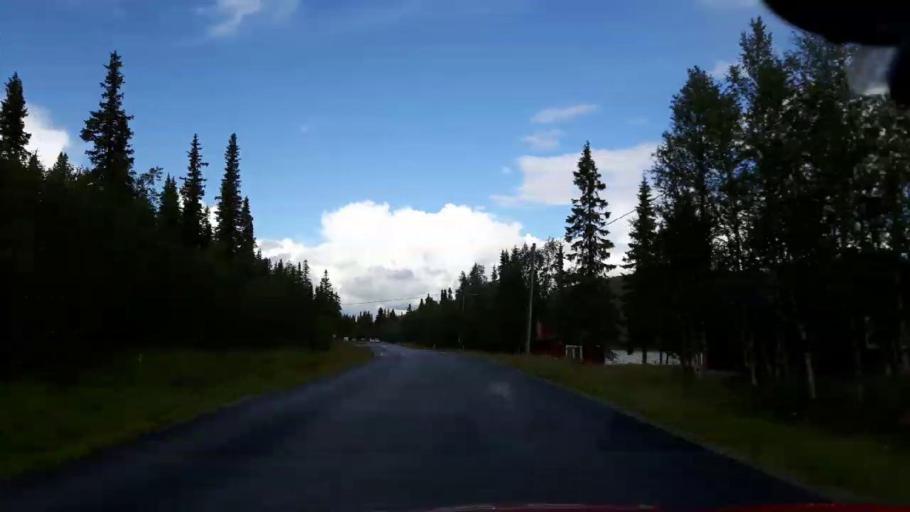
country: SE
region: Vaesterbotten
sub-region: Vilhelmina Kommun
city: Sjoberg
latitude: 65.0198
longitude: 15.1654
